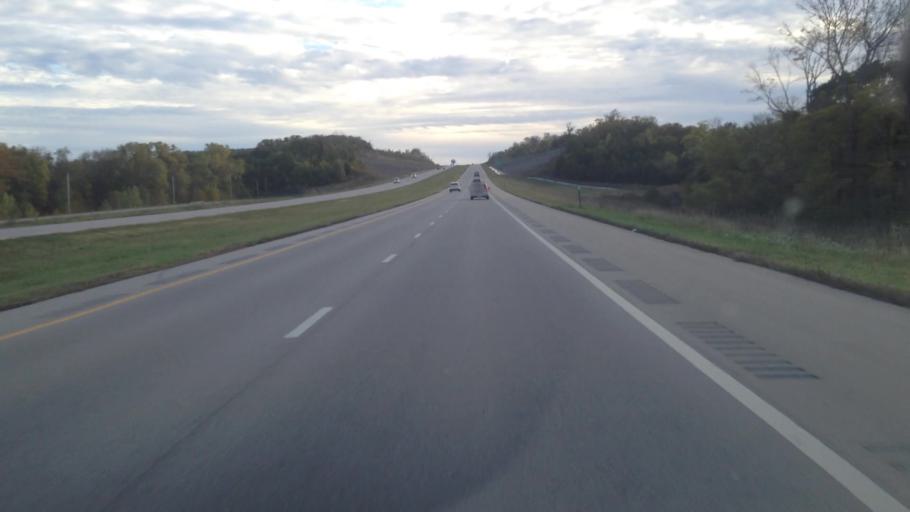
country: US
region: Kansas
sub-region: Douglas County
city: Baldwin City
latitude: 38.8597
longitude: -95.2608
